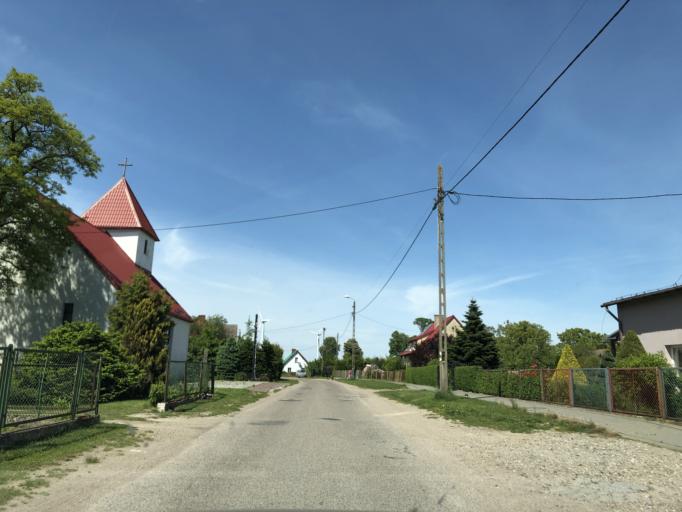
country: PL
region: West Pomeranian Voivodeship
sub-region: Powiat kolobrzeski
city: Goscino
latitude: 54.0494
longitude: 15.7288
